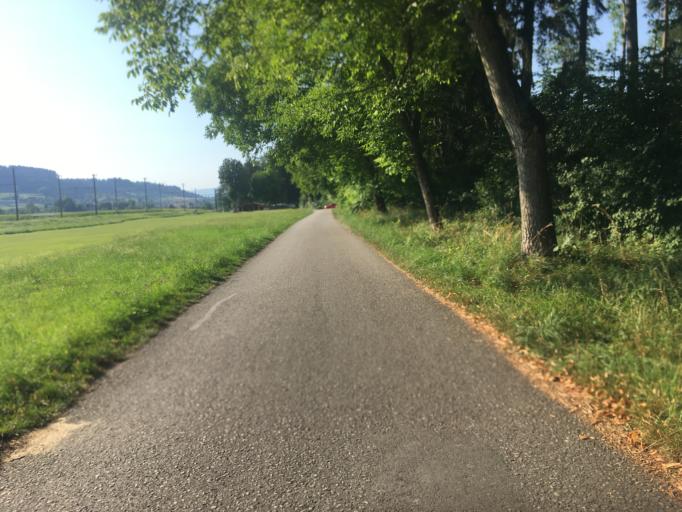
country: CH
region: Bern
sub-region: Emmental District
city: Oberburg
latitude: 47.0214
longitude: 7.6473
